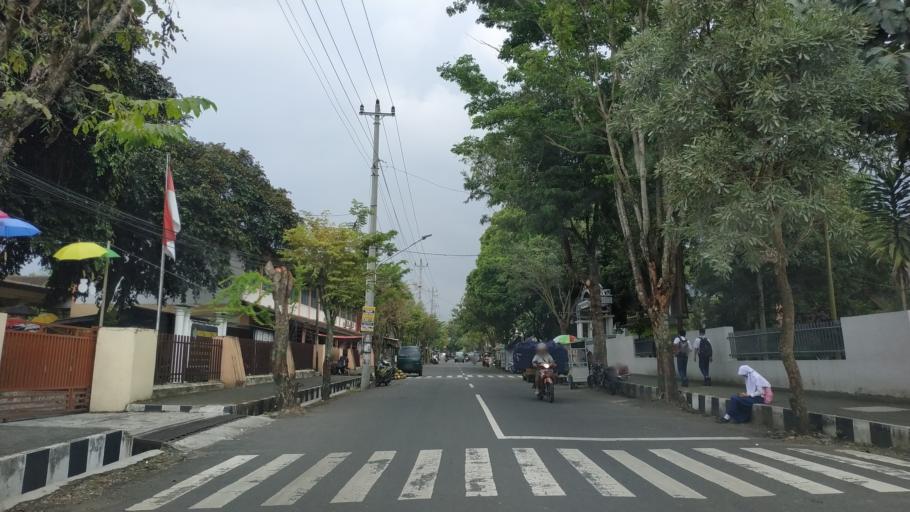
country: ID
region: Central Java
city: Magelang
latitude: -7.3114
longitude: 110.1772
